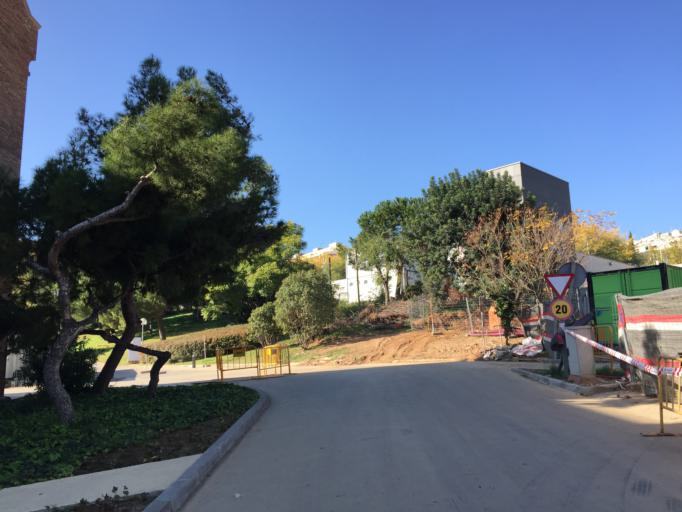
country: ES
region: Catalonia
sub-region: Provincia de Barcelona
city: Horta-Guinardo
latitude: 41.4140
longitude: 2.1736
